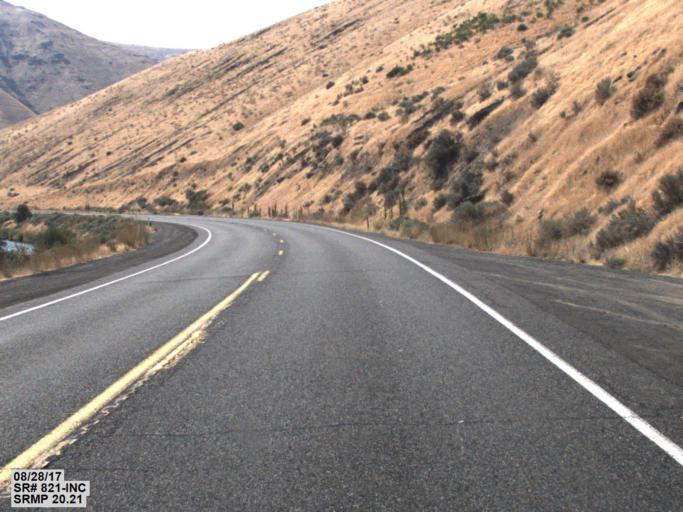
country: US
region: Washington
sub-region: Kittitas County
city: Kittitas
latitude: 46.8855
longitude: -120.4803
